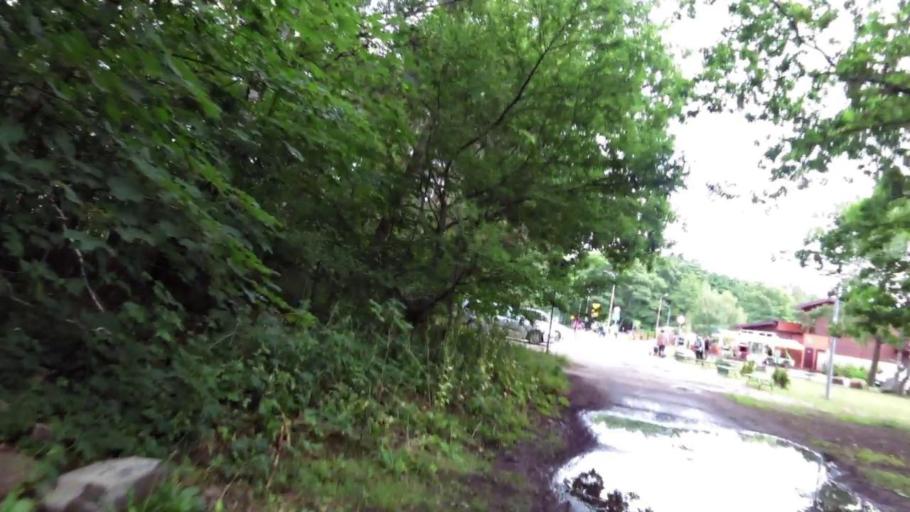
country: PL
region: West Pomeranian Voivodeship
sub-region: Powiat slawienski
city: Darlowo
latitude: 54.5071
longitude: 16.4657
